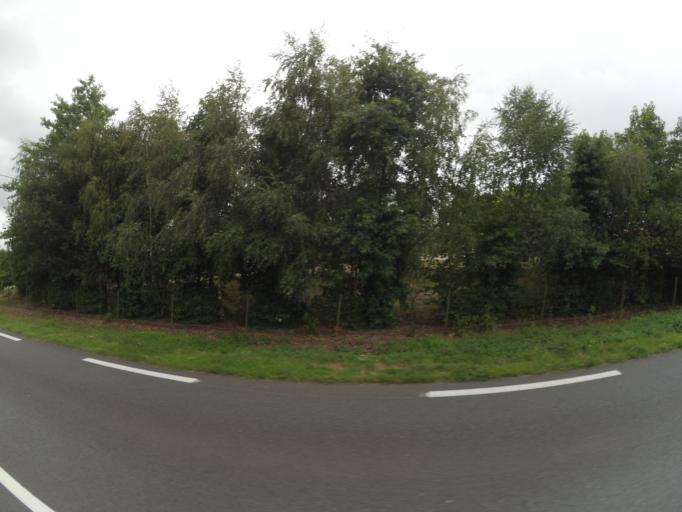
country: FR
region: Pays de la Loire
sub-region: Departement de la Vendee
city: Froidfond
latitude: 46.8721
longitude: -1.7464
